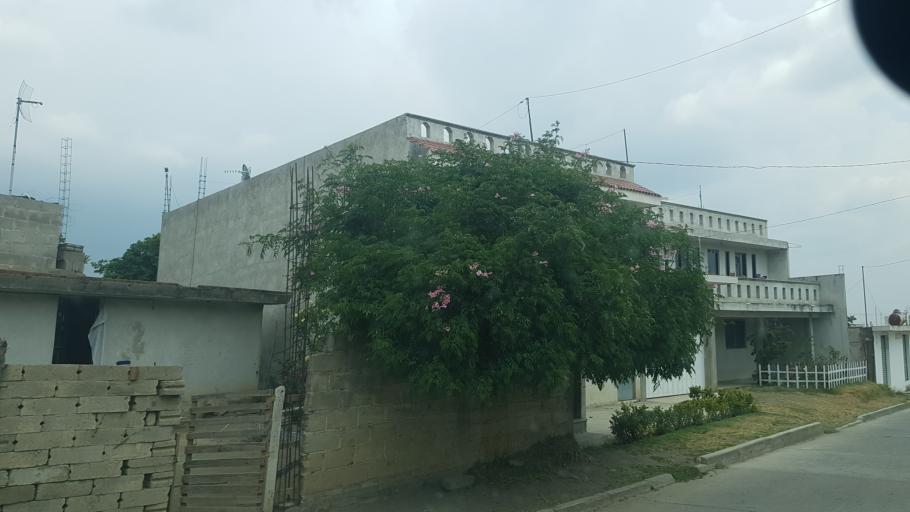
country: MX
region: Puebla
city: Domingo Arenas
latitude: 19.1519
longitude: -98.4916
